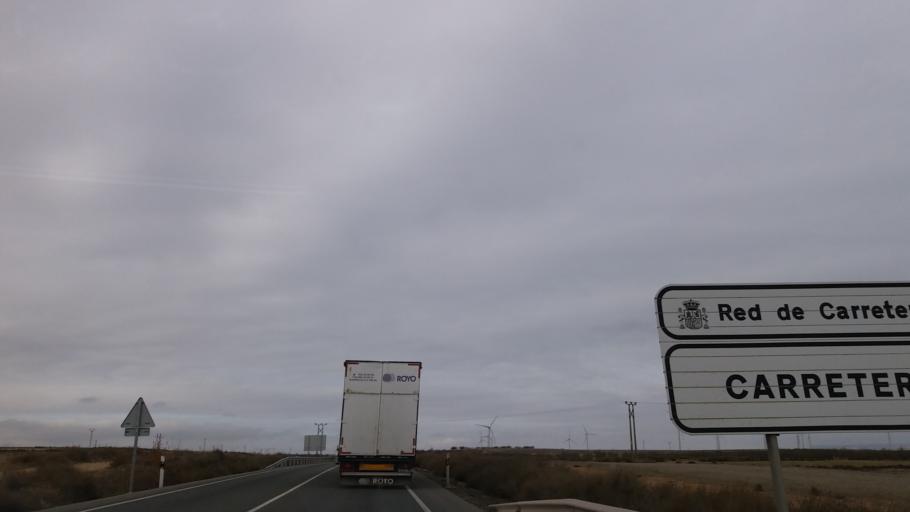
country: ES
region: Aragon
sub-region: Provincia de Zaragoza
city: Mallen
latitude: 41.8632
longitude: -1.3833
